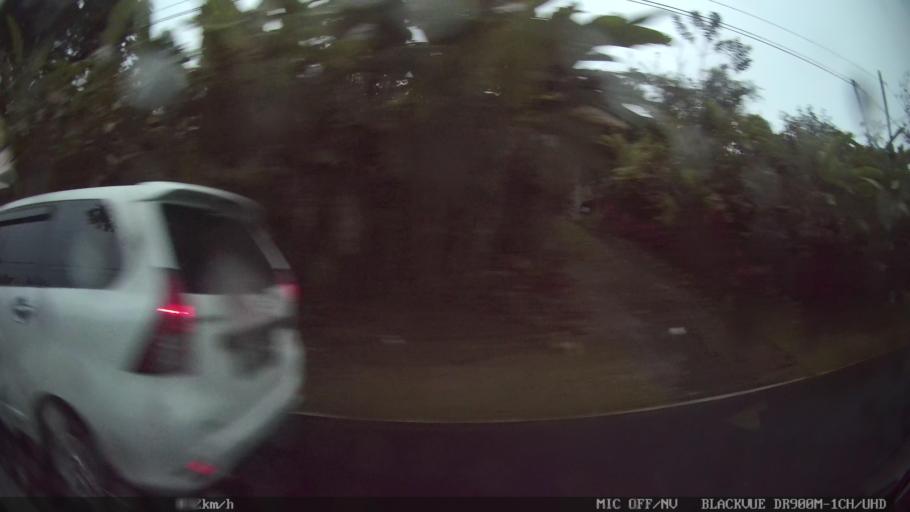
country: ID
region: Bali
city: Banjar Taro Kelod
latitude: -8.3645
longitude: 115.2708
